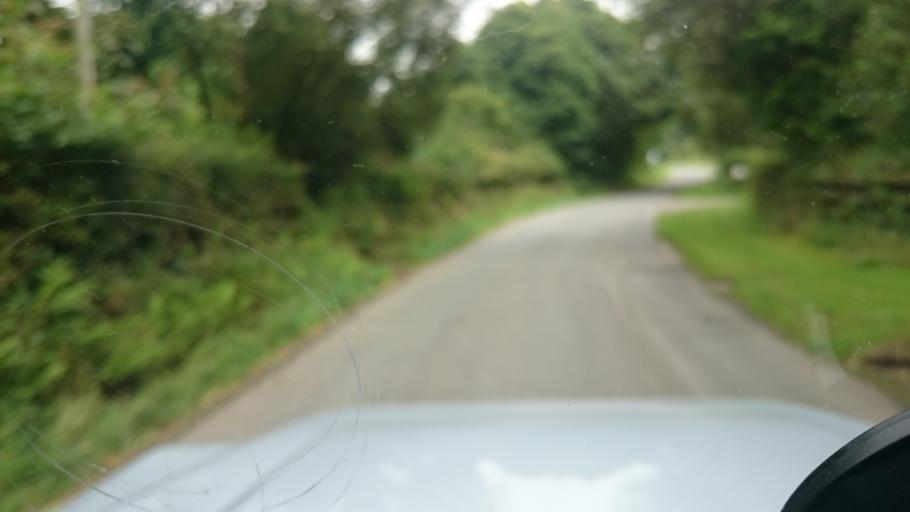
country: GB
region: Wales
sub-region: Pembrokeshire
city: Ambleston
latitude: 51.9260
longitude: -4.9520
